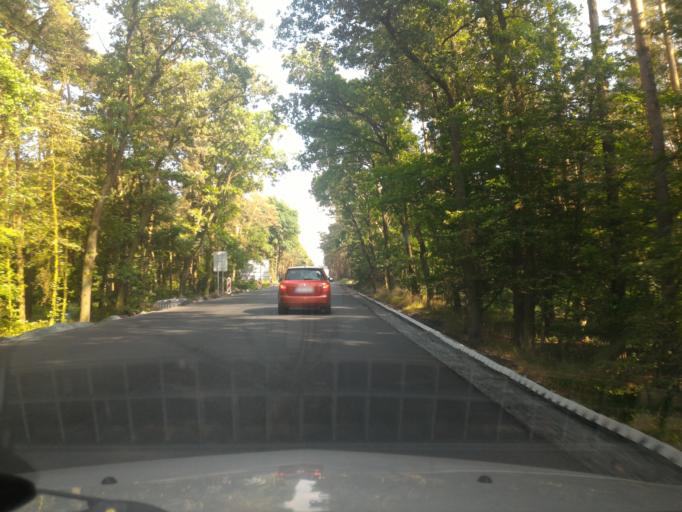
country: CZ
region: Central Bohemia
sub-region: Okres Nymburk
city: Podebrady
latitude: 50.1124
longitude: 15.1312
